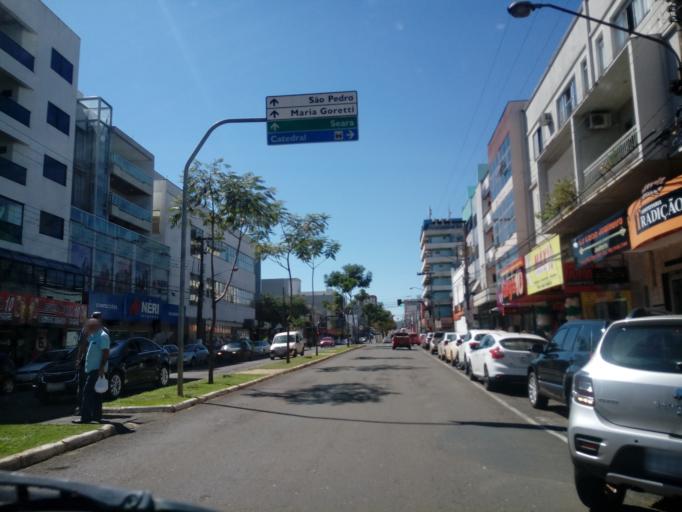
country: BR
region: Santa Catarina
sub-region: Chapeco
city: Chapeco
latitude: -27.1007
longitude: -52.6164
